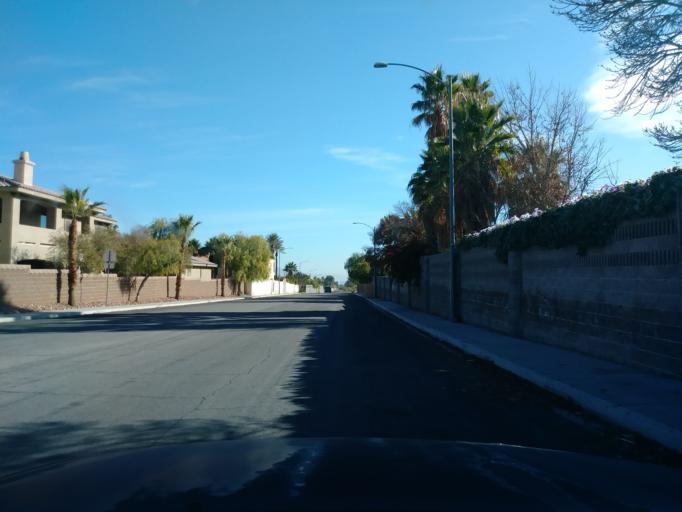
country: US
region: Nevada
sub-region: Clark County
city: Spring Valley
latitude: 36.1496
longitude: -115.2748
